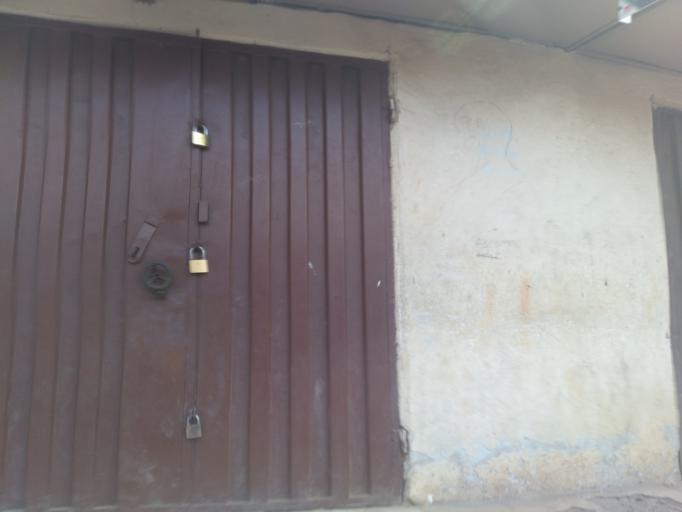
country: GH
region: Ashanti
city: Kumasi
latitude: 6.6951
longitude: -1.6141
